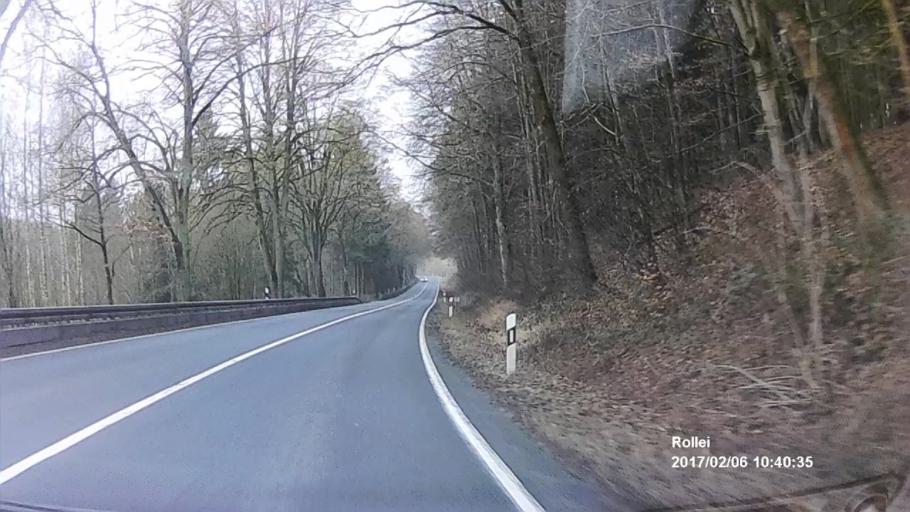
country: DE
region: Lower Saxony
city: Wulften
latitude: 51.7101
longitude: 10.1797
